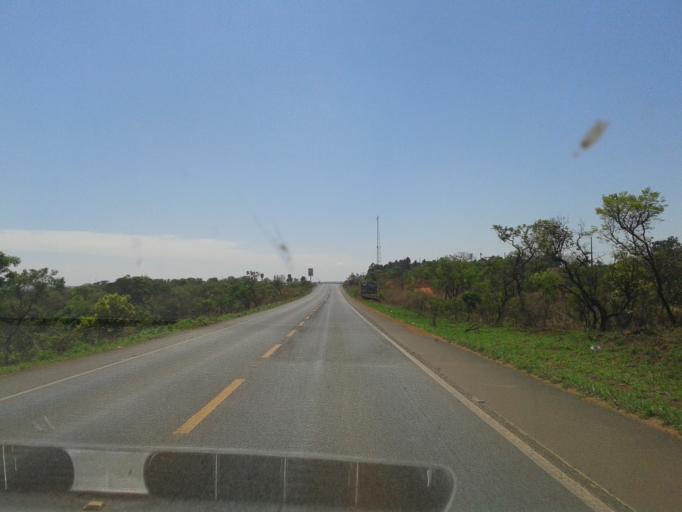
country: BR
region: Minas Gerais
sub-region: Sacramento
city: Sacramento
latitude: -19.3199
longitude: -47.5526
